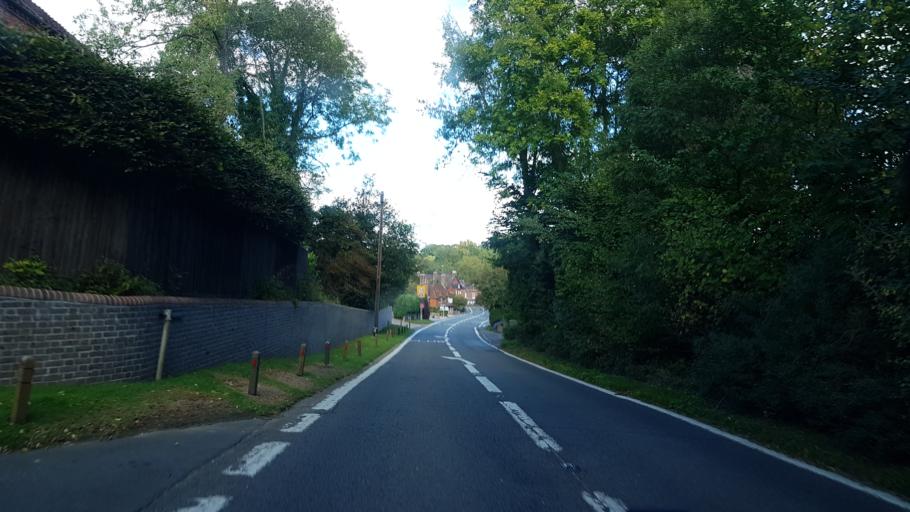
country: GB
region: England
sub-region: Surrey
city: Chiddingfold
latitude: 51.1073
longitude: -0.6308
